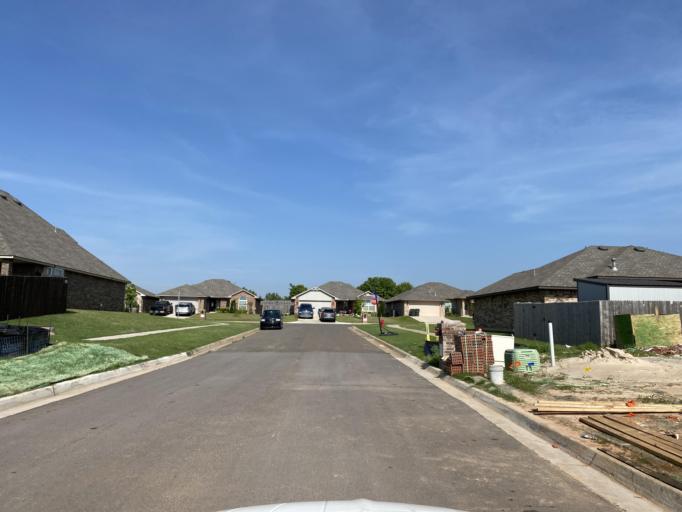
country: US
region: Oklahoma
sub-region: Oklahoma County
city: Nicoma Park
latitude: 35.4384
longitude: -97.3415
